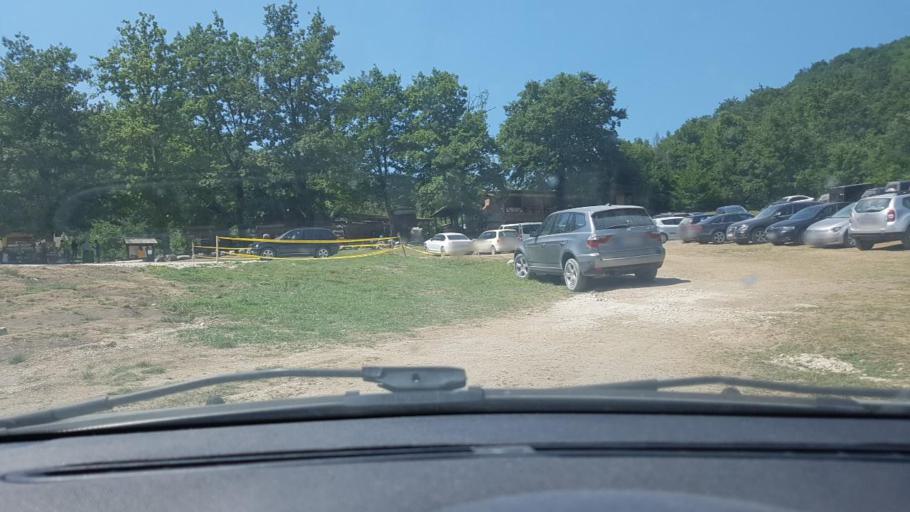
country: BA
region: Federation of Bosnia and Herzegovina
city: Orasac
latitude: 44.6564
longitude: 16.0129
